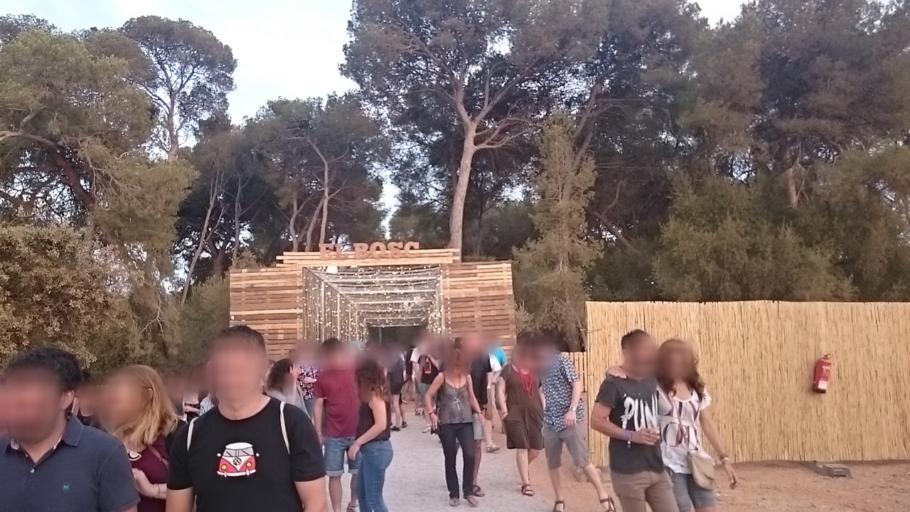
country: ES
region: Catalonia
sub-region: Provincia de Barcelona
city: Vilanova i la Geltru
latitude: 41.2395
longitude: 1.7149
